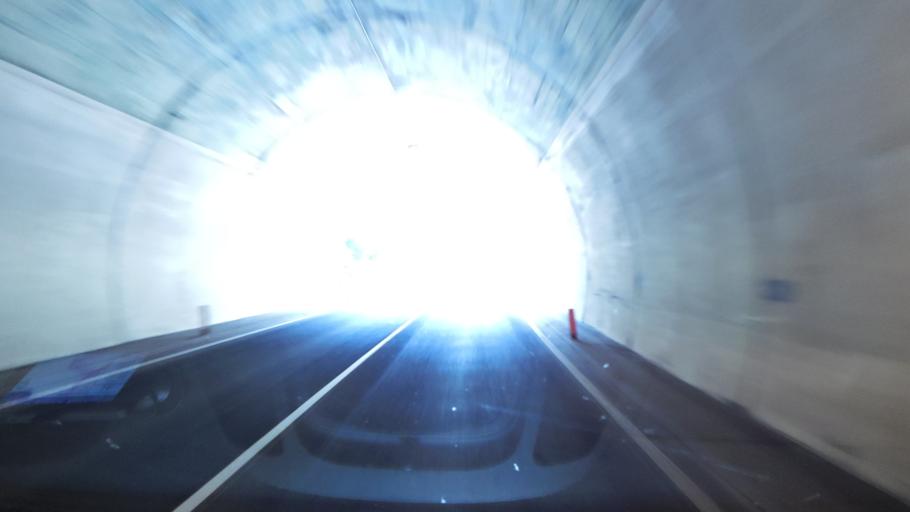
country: AT
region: Salzburg
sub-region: Politischer Bezirk Hallein
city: Scheffau am Tennengebirge
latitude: 47.5761
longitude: 13.1949
